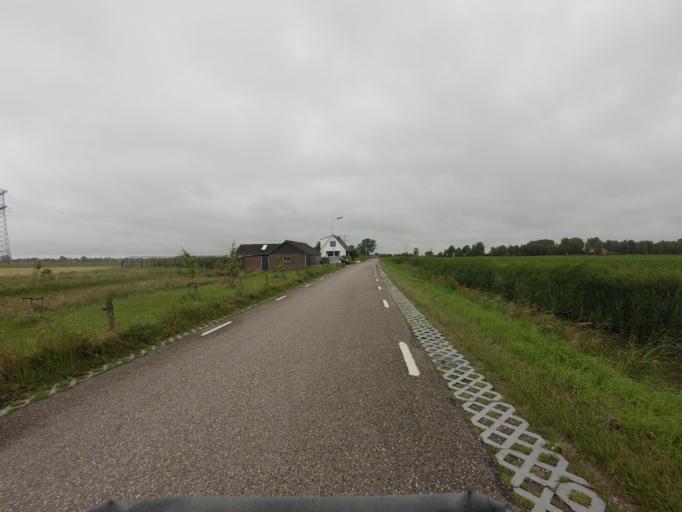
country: NL
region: North Holland
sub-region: Gemeente Schagen
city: Schagen
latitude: 52.7802
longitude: 4.8279
